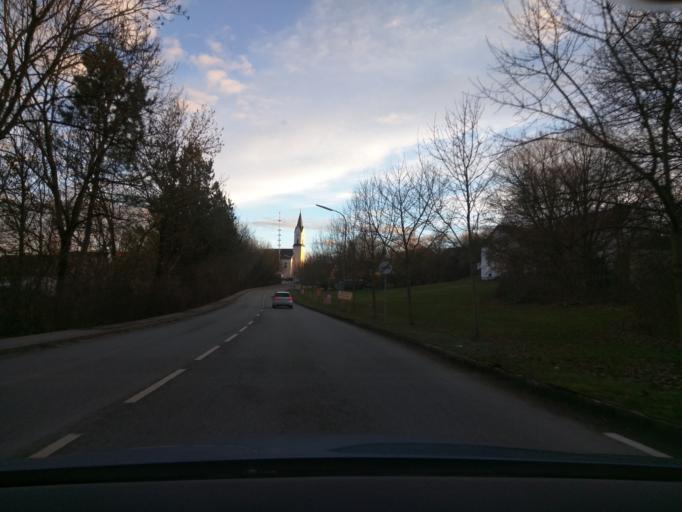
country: DE
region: Bavaria
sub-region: Upper Bavaria
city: Attenkirchen
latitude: 48.5086
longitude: 11.7575
